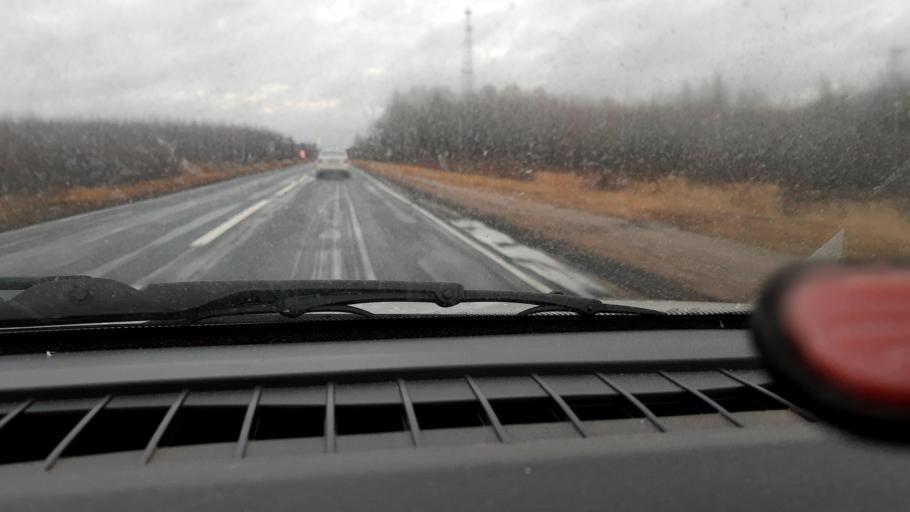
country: RU
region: Nizjnij Novgorod
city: Krasnyye Baki
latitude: 57.0952
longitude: 45.1538
